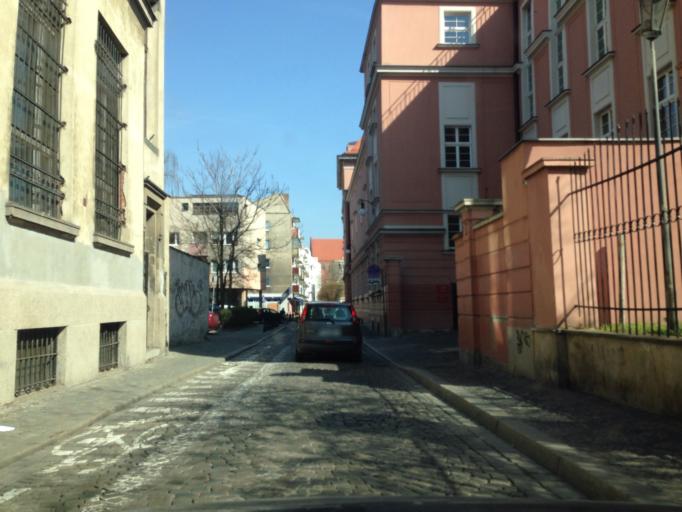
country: PL
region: Lower Silesian Voivodeship
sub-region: Powiat wroclawski
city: Wroclaw
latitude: 51.1101
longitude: 17.0373
